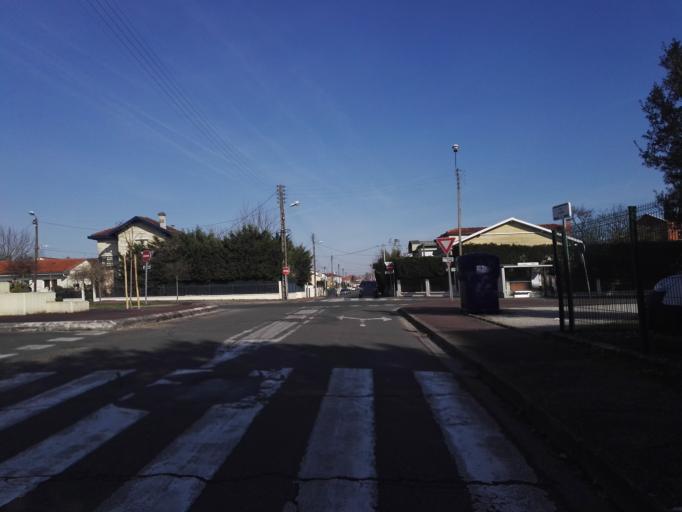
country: FR
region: Aquitaine
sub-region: Departement de la Gironde
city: Talence
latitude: 44.7987
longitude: -0.5875
